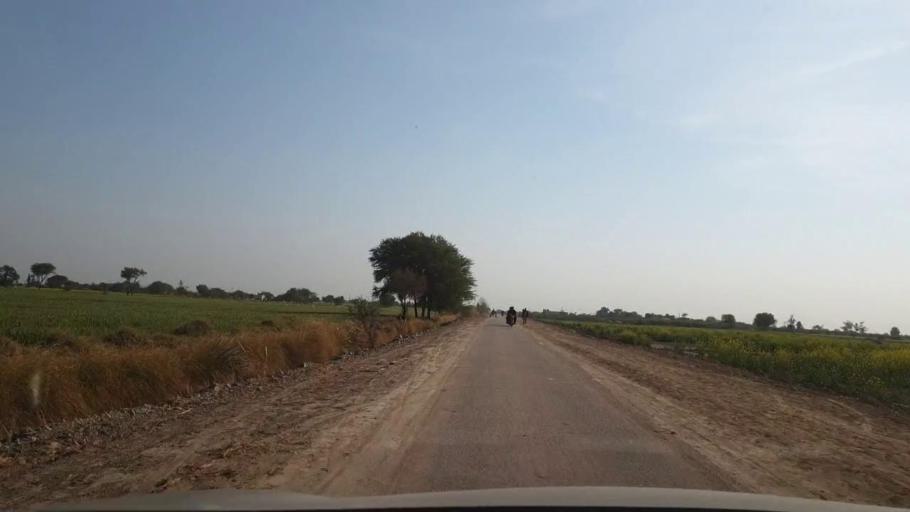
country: PK
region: Sindh
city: Berani
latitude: 25.7327
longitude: 68.8067
